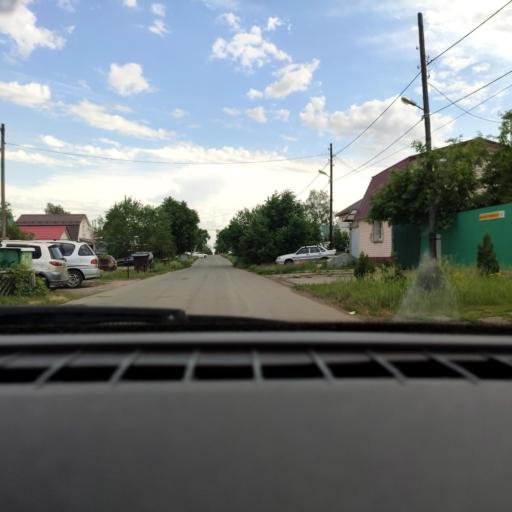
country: RU
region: Samara
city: Petra-Dubrava
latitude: 53.2642
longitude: 50.3302
